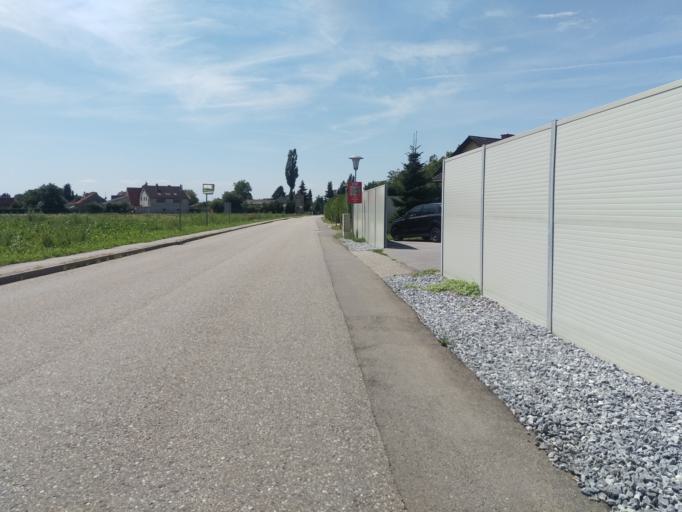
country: AT
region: Styria
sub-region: Politischer Bezirk Graz-Umgebung
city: Feldkirchen bei Graz
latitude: 47.0115
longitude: 15.4302
